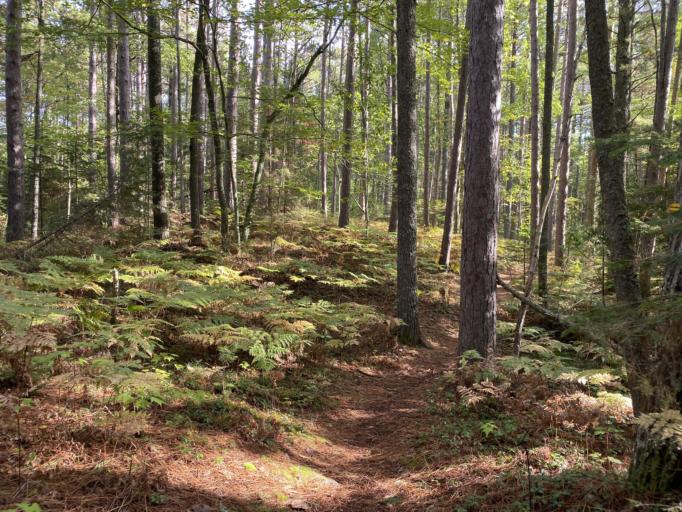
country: US
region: Michigan
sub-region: Mackinac County
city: Saint Ignace
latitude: 45.7433
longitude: -84.8834
